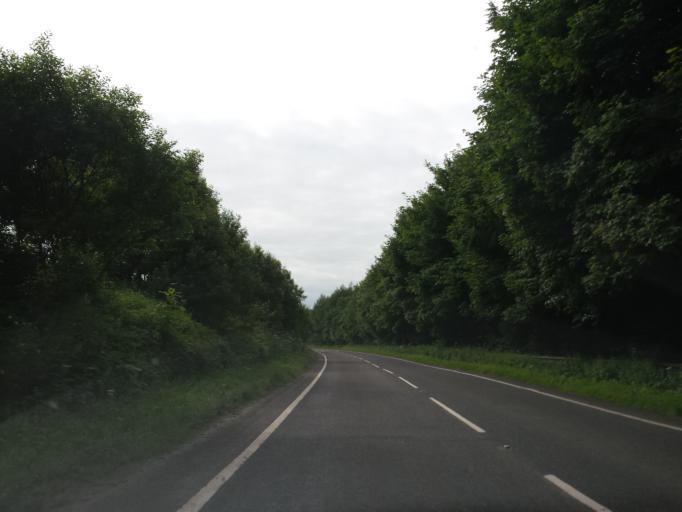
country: GB
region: Scotland
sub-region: Dumfries and Galloway
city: Moffat
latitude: 55.3194
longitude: -3.4664
